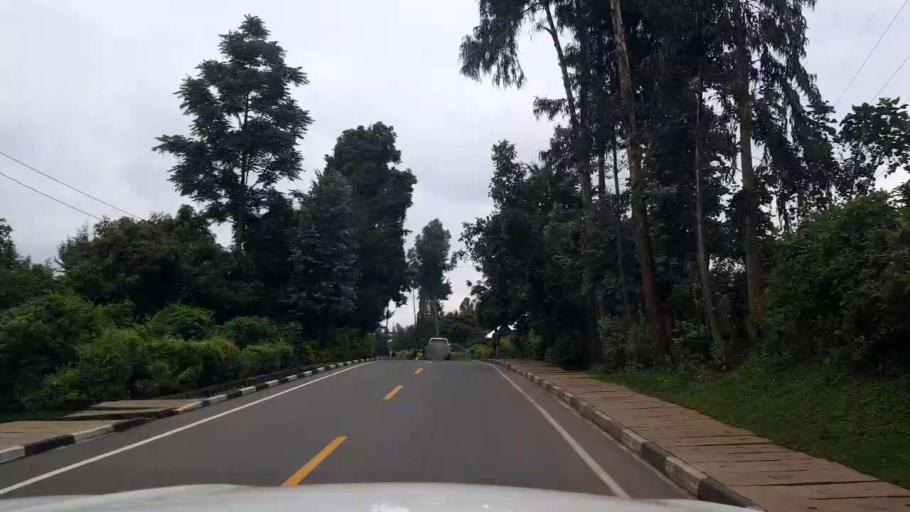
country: RW
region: Northern Province
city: Musanze
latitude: -1.4504
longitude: 29.5931
